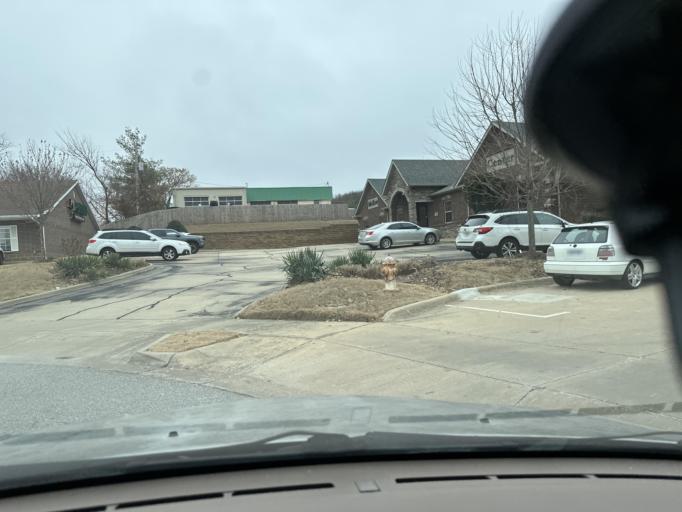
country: US
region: Arkansas
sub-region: Washington County
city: Johnson
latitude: 36.1041
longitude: -94.1490
